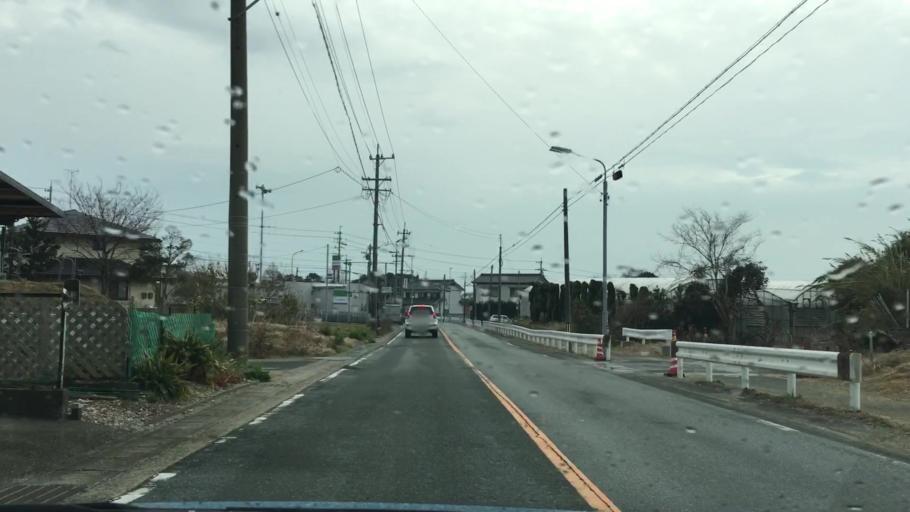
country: JP
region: Aichi
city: Tahara
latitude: 34.6966
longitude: 137.2759
